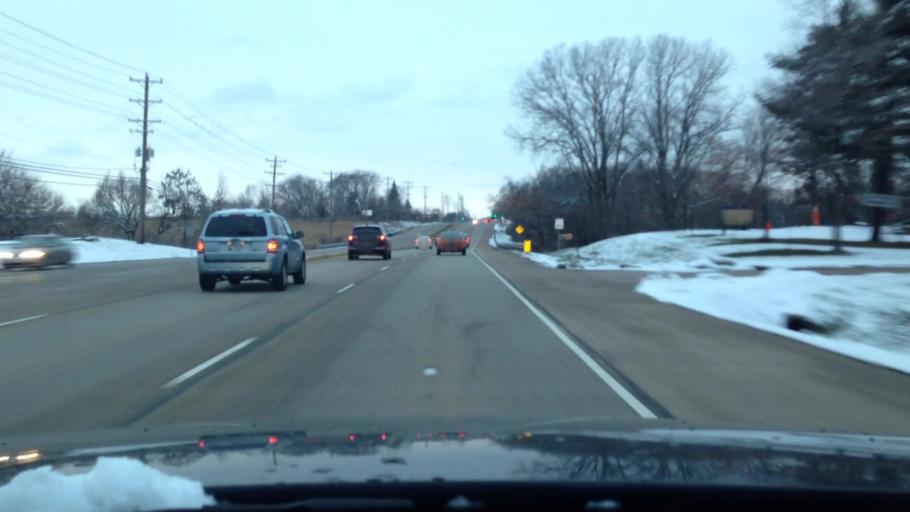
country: US
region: Illinois
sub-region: McHenry County
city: Lake in the Hills
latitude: 42.1758
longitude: -88.3738
